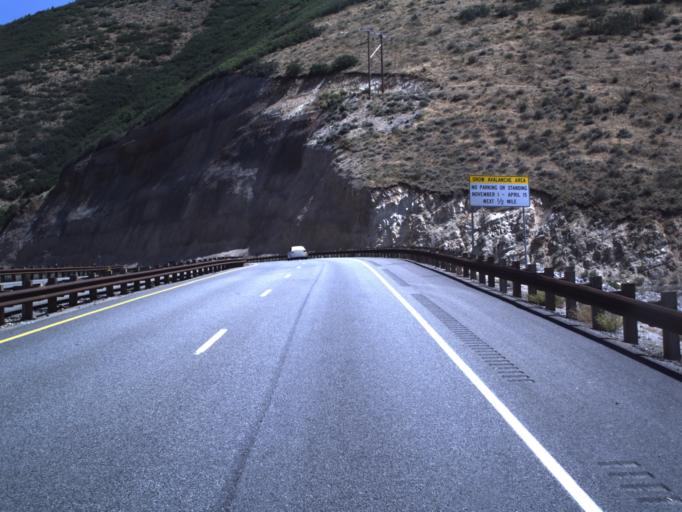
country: US
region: Utah
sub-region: Wasatch County
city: Midway
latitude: 40.4058
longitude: -111.5278
